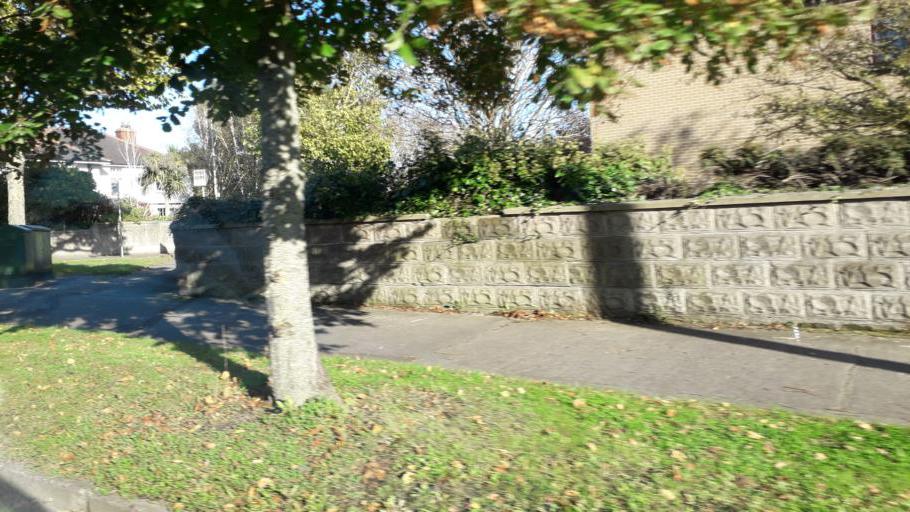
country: IE
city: Killester
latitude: 53.3670
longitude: -6.1949
